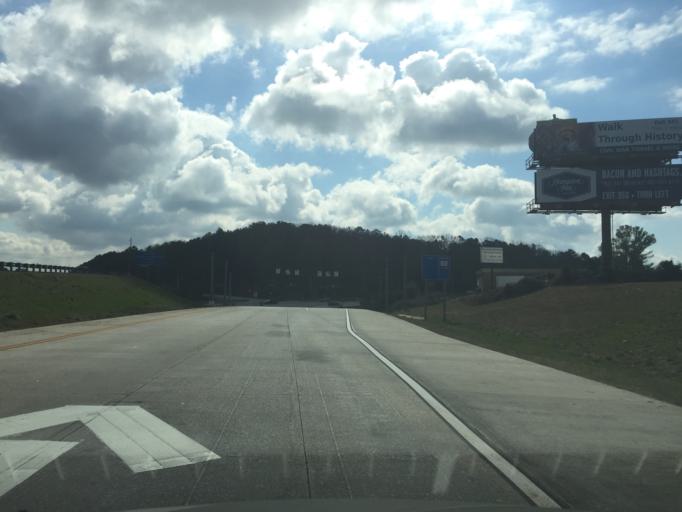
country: US
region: Georgia
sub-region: Catoosa County
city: Indian Springs
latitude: 34.9689
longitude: -85.1927
